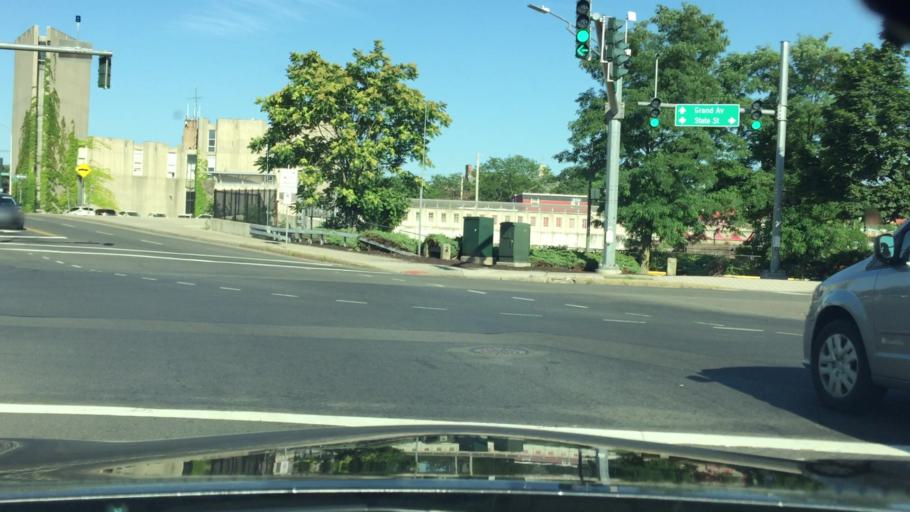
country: US
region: Connecticut
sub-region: New Haven County
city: New Haven
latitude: 41.3071
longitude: -72.9213
